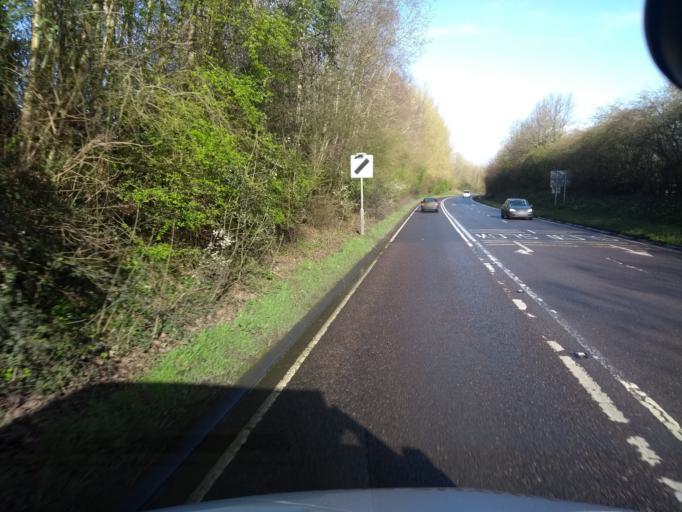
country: GB
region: England
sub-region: Somerset
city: Yeovil
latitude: 50.9575
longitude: -2.6500
